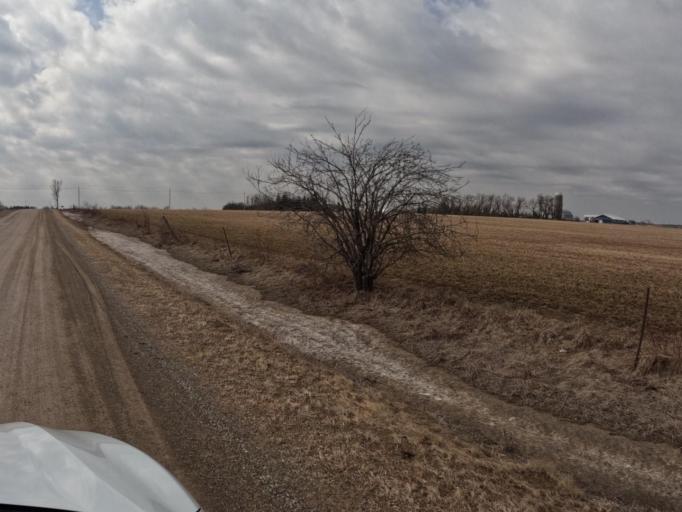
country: CA
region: Ontario
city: Orangeville
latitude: 43.9235
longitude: -80.2187
